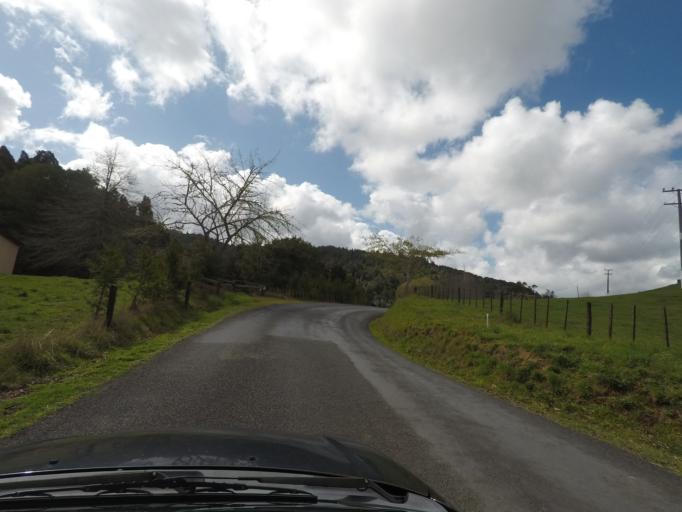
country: NZ
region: Auckland
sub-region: Auckland
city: Red Hill
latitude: -37.1173
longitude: 175.1133
